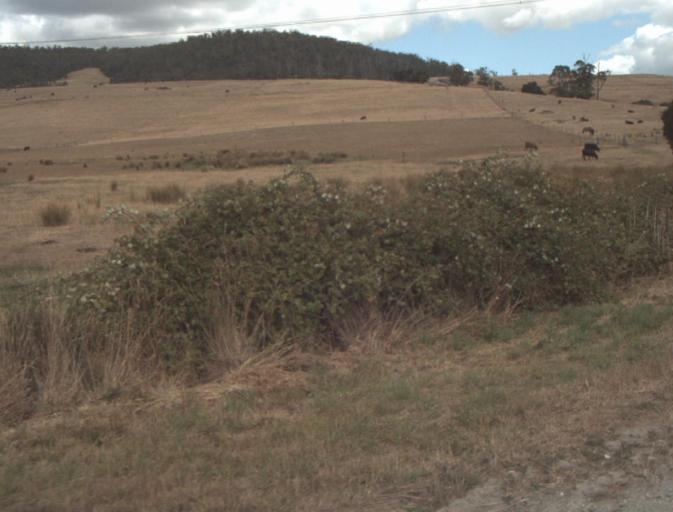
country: AU
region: Tasmania
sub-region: Launceston
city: Mayfield
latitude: -41.2037
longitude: 147.0788
